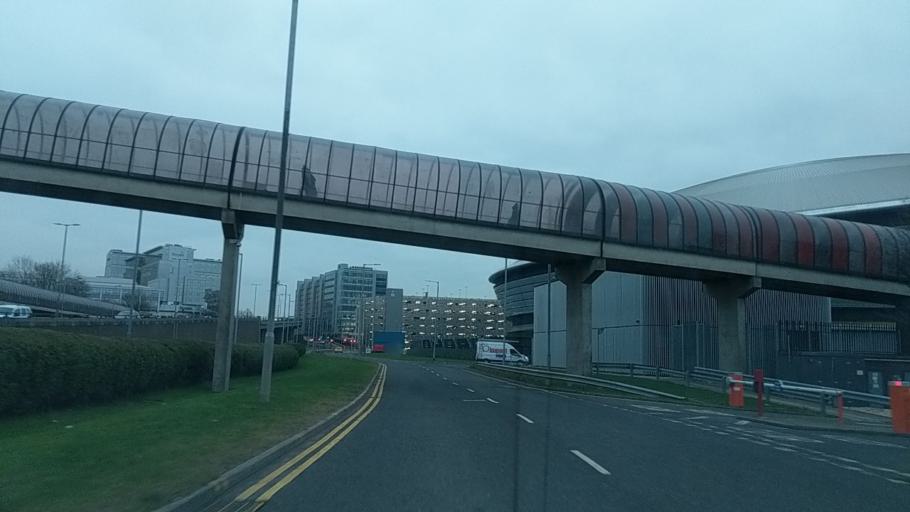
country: GB
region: Scotland
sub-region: Glasgow City
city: Glasgow
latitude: 55.8615
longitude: -4.2866
